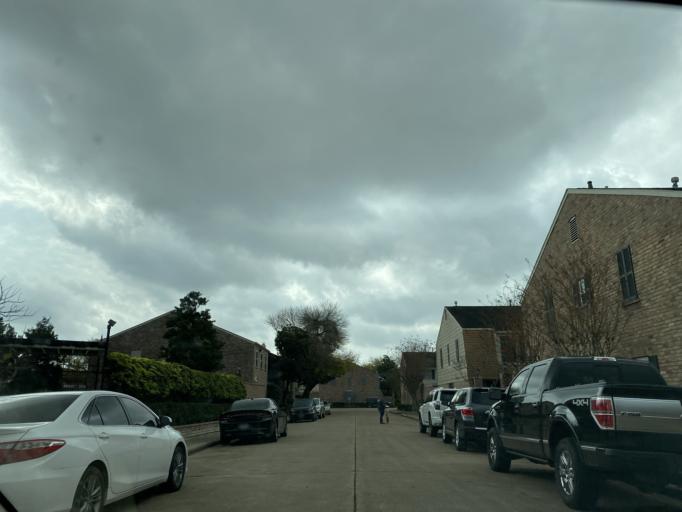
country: US
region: Texas
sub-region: Harris County
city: Piney Point Village
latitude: 29.7430
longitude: -95.4990
